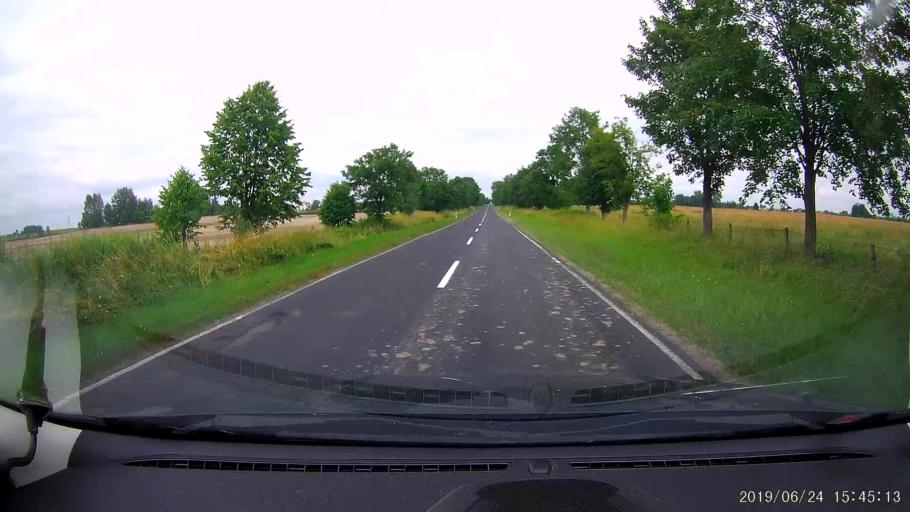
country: PL
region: Subcarpathian Voivodeship
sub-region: Powiat lubaczowski
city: Oleszyce
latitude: 50.1454
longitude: 22.9773
